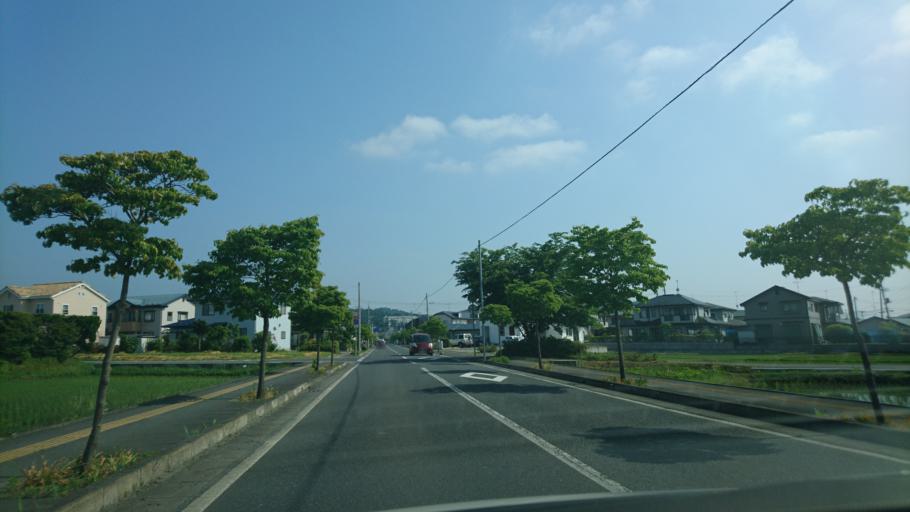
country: JP
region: Iwate
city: Ichinoseki
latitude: 38.9305
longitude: 141.1126
